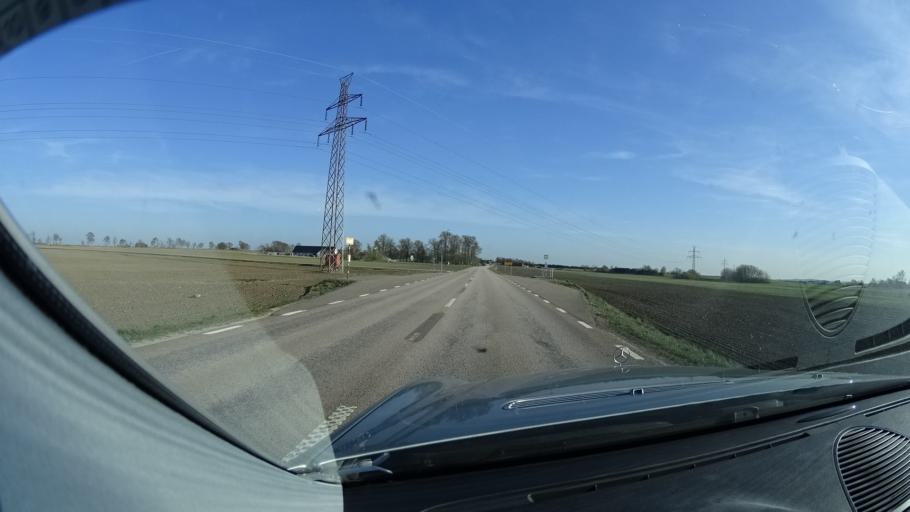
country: SE
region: Skane
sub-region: Landskrona
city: Asmundtorp
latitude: 55.9716
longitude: 12.9401
